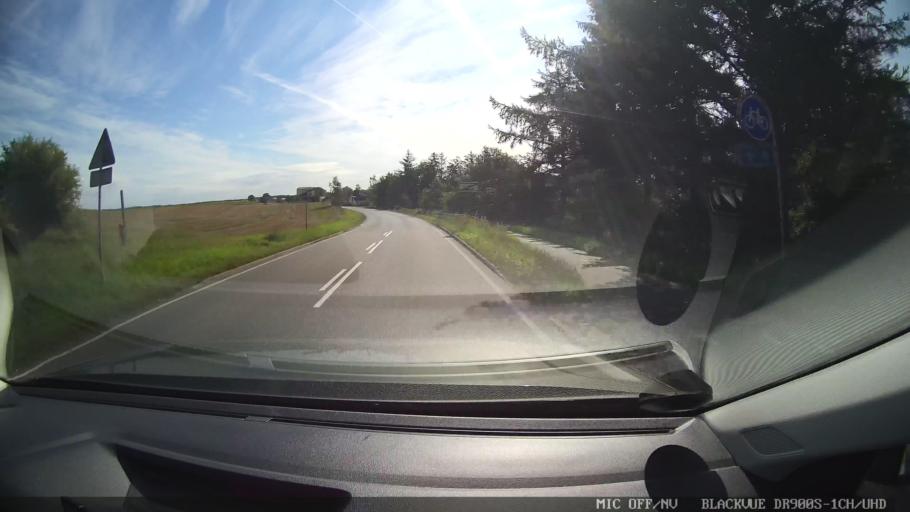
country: DK
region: North Denmark
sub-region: Mariagerfjord Kommune
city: Arden
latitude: 56.7642
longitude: 9.8724
